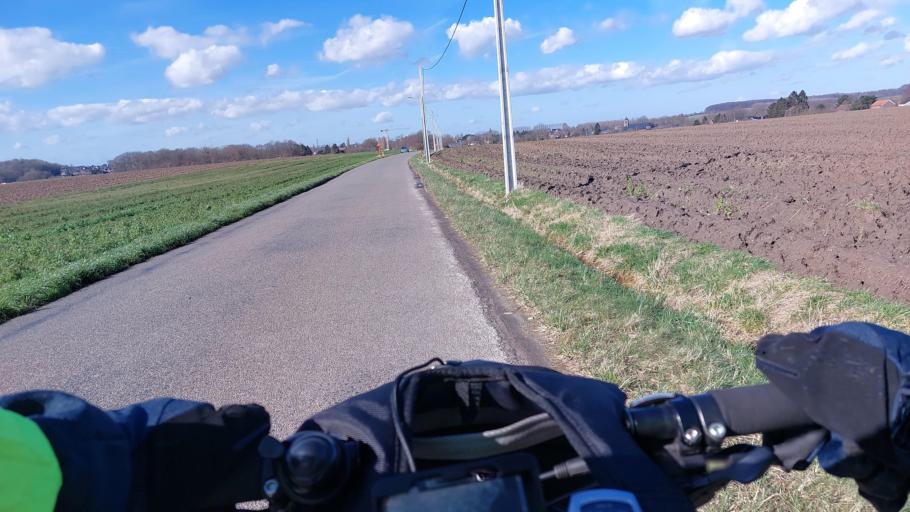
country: BE
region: Wallonia
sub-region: Province du Hainaut
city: Ecaussinnes-d'Enghien
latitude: 50.5634
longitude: 4.1864
